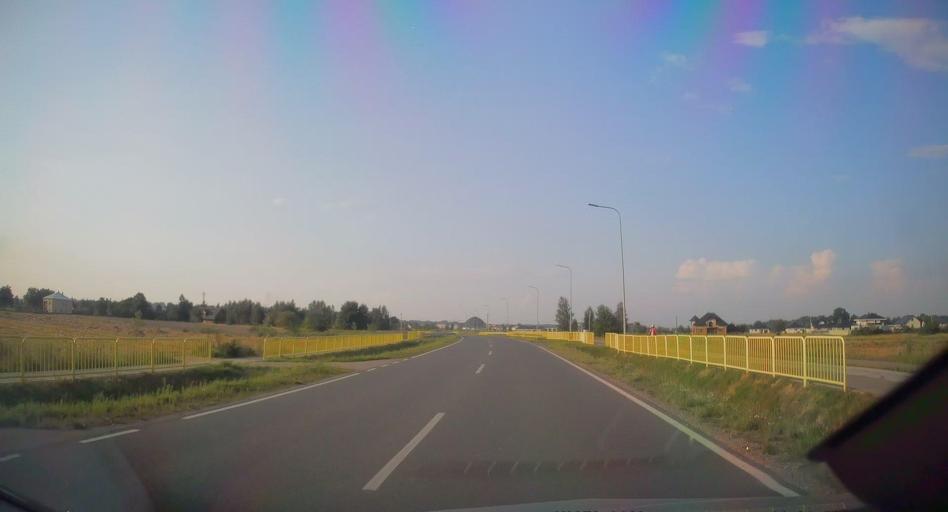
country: PL
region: Subcarpathian Voivodeship
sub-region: Powiat debicki
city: Zyrakow
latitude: 50.0694
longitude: 21.3805
